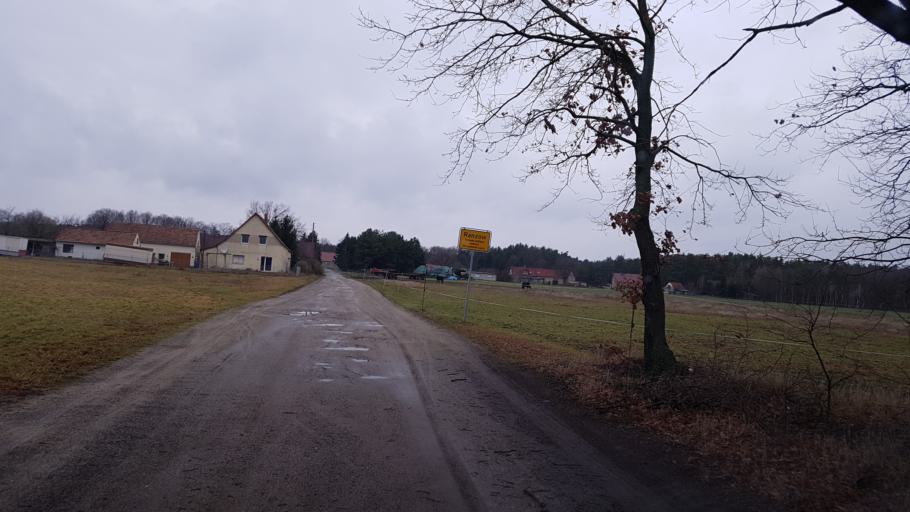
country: DE
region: Brandenburg
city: Altdobern
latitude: 51.6908
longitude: 14.0445
